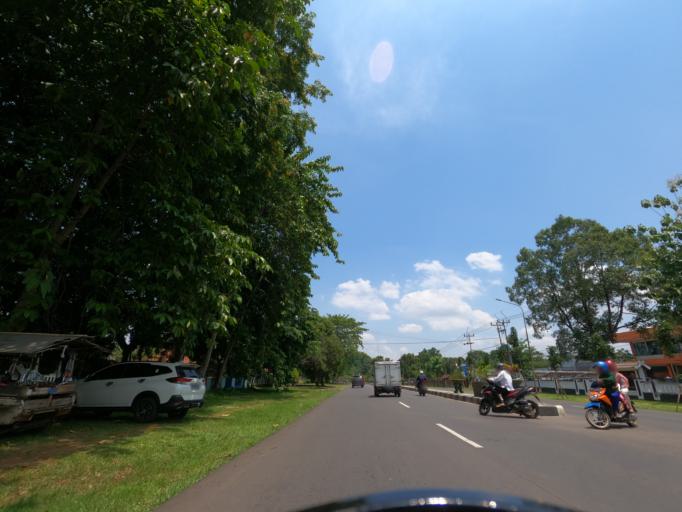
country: ID
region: West Java
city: Pamanukan
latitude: -6.5543
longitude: 107.7627
